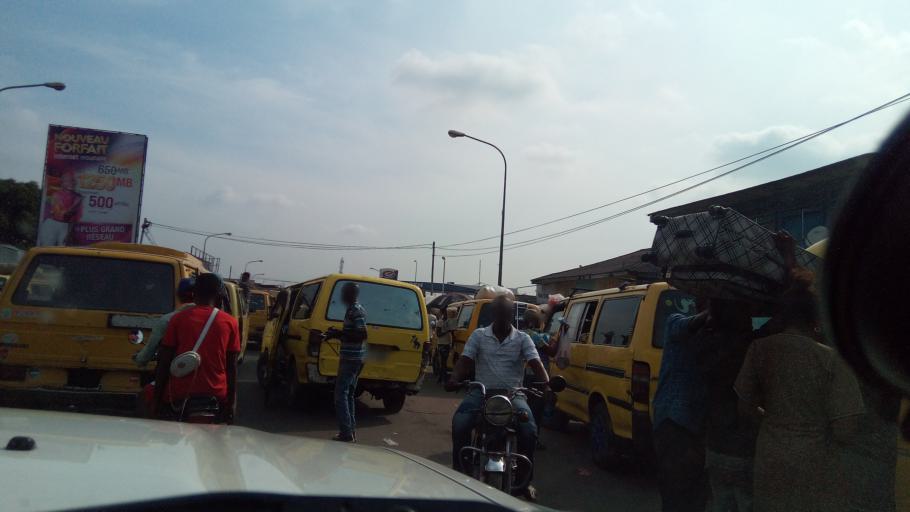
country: CD
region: Kinshasa
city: Kinshasa
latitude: -4.3479
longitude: 15.3115
